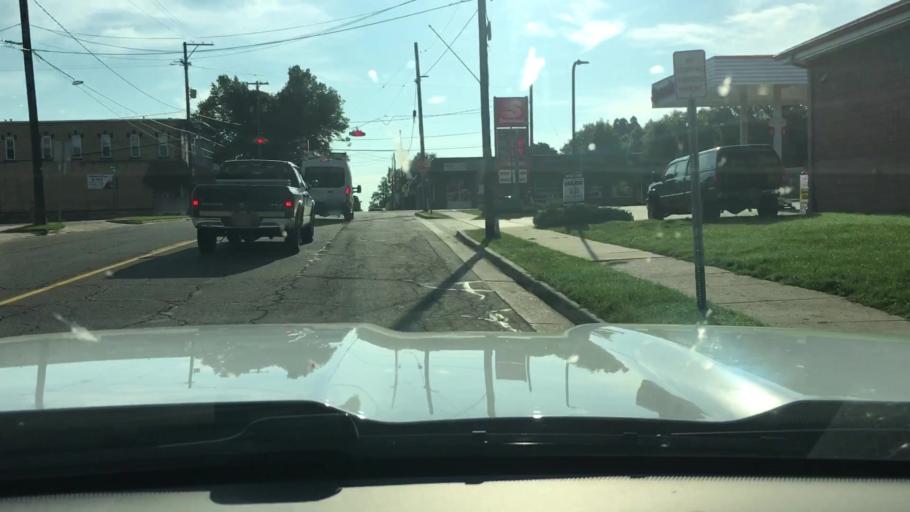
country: US
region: Michigan
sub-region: Kent County
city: Kent City
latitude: 43.2195
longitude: -85.7522
